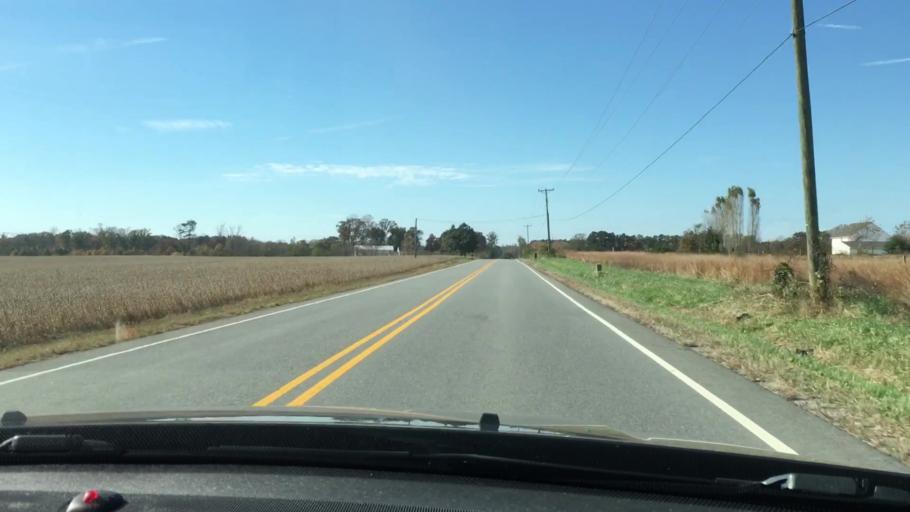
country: US
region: Virginia
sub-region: King and Queen County
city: King and Queen Court House
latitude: 37.5912
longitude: -76.8873
